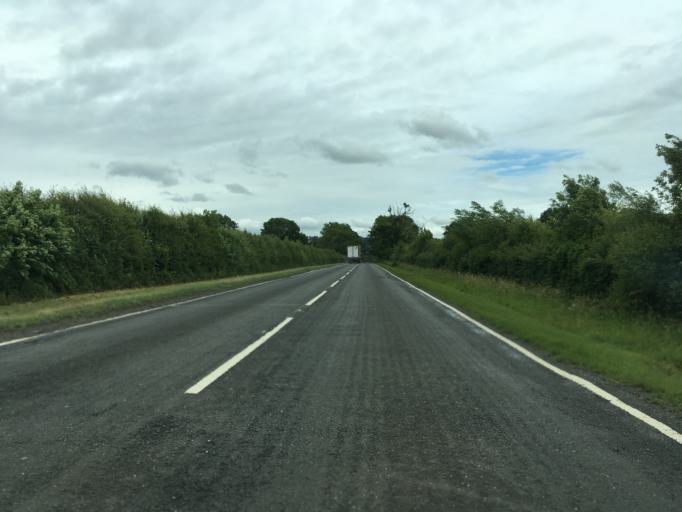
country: GB
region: England
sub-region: Northamptonshire
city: Daventry
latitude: 52.2509
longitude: -1.2448
